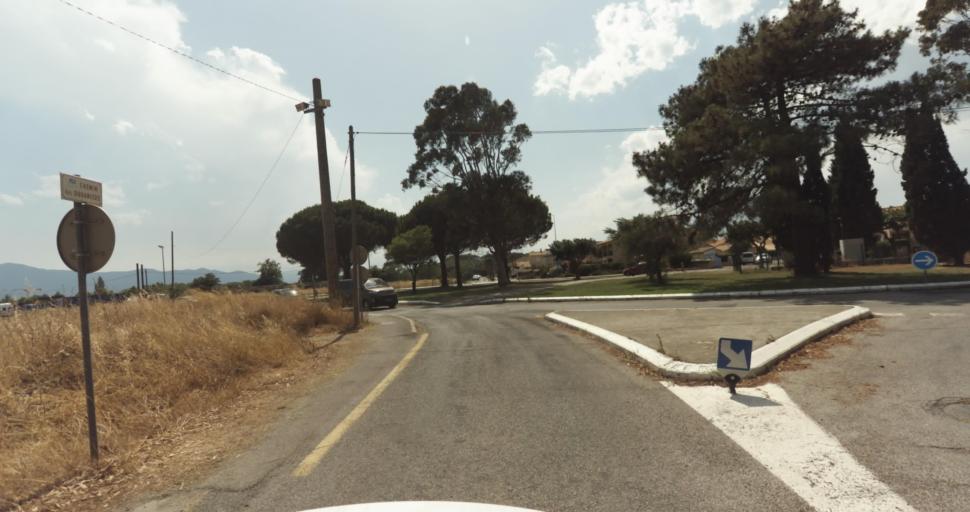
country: FR
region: Languedoc-Roussillon
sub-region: Departement des Pyrenees-Orientales
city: Saint-Cyprien-Plage
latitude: 42.6187
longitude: 3.0337
